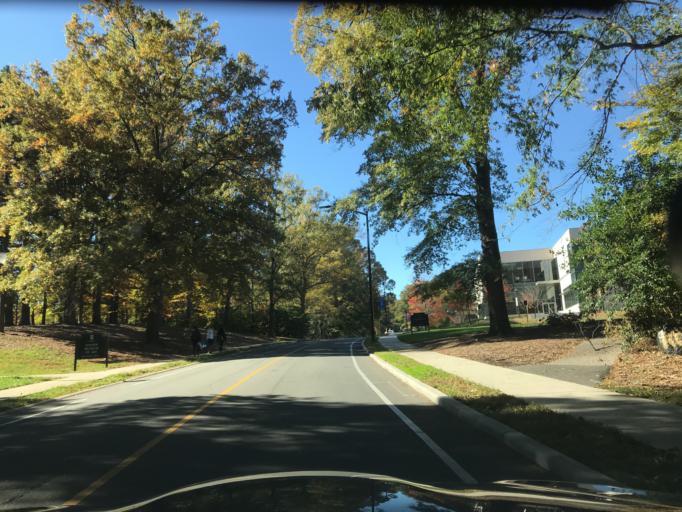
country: US
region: North Carolina
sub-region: Durham County
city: Durham
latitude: 35.9999
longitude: -78.9280
